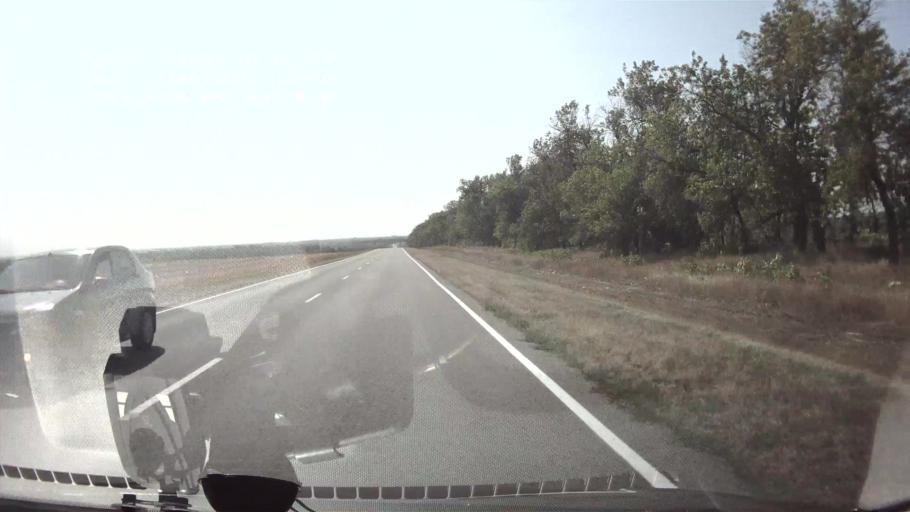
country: RU
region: Krasnodarskiy
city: Dmitriyevskaya
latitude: 45.7614
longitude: 40.7192
